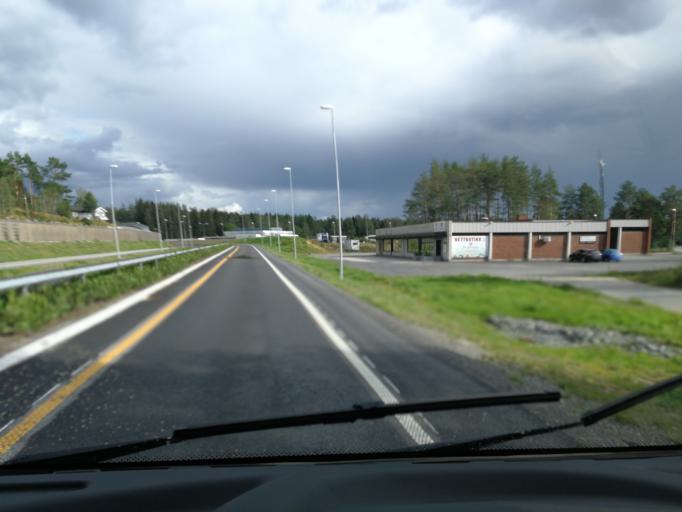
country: NO
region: Ostfold
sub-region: Marker
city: Orje
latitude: 59.4797
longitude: 11.6693
